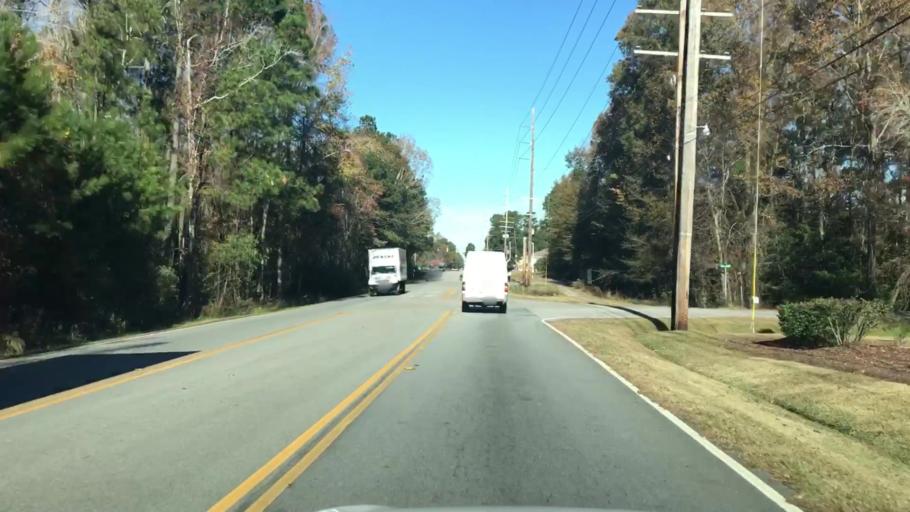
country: US
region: South Carolina
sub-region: Dorchester County
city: Centerville
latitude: 32.9878
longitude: -80.2218
